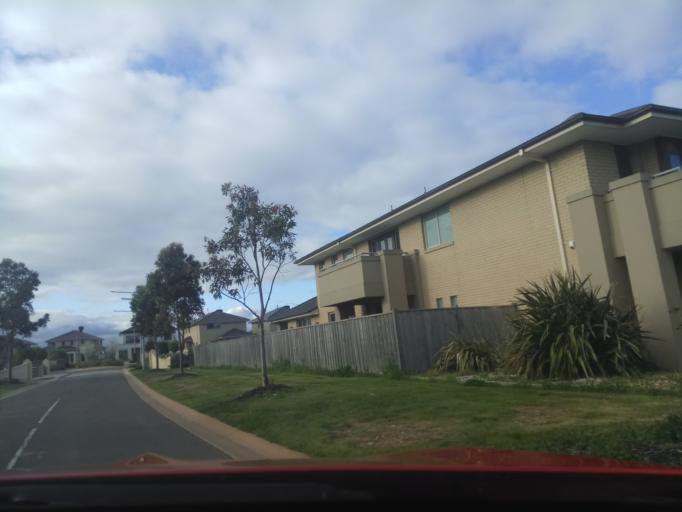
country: AU
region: Victoria
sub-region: Hobsons Bay
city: Altona Meadows
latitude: -37.9026
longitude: 144.7705
